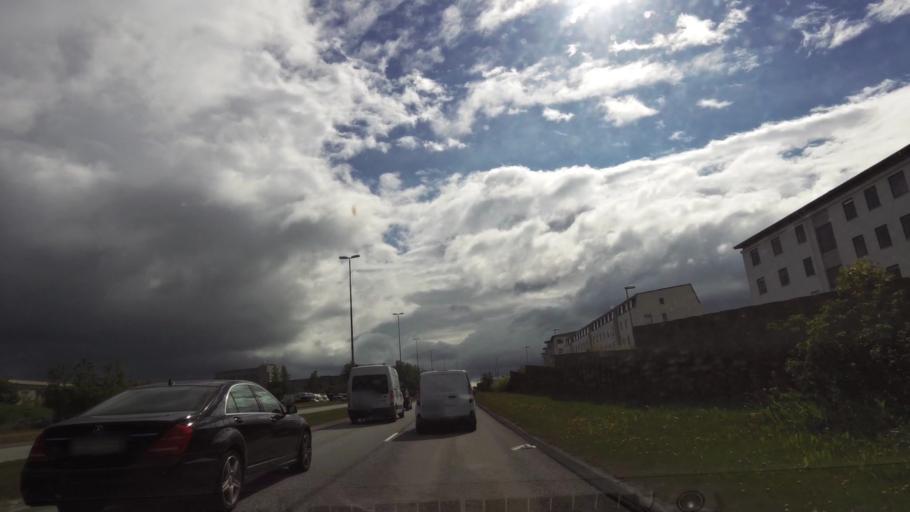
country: IS
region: Capital Region
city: Reykjavik
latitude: 64.1511
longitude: -21.8776
